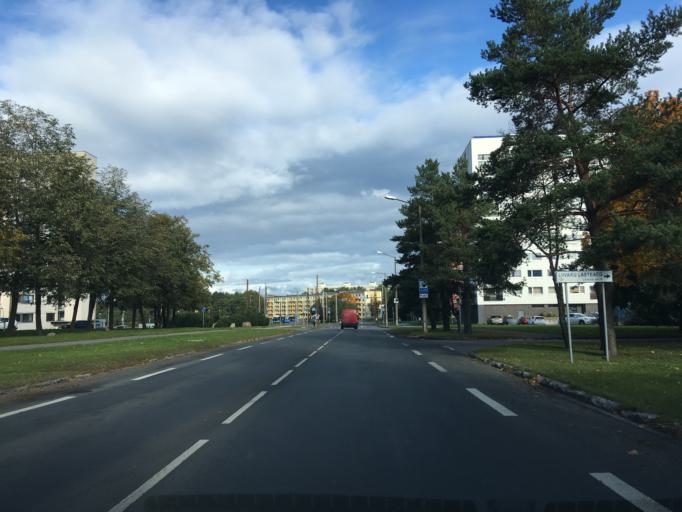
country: EE
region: Harju
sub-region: Tallinna linn
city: Tallinn
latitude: 59.3974
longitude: 24.6819
